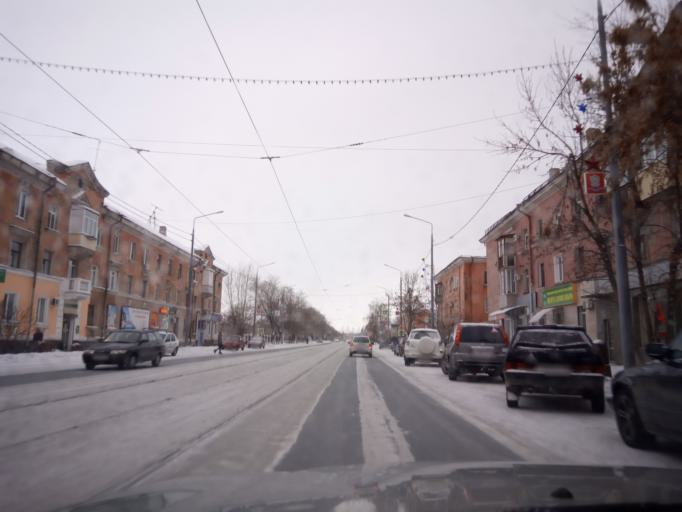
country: RU
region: Orenburg
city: Novotroitsk
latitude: 51.1958
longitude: 58.3213
